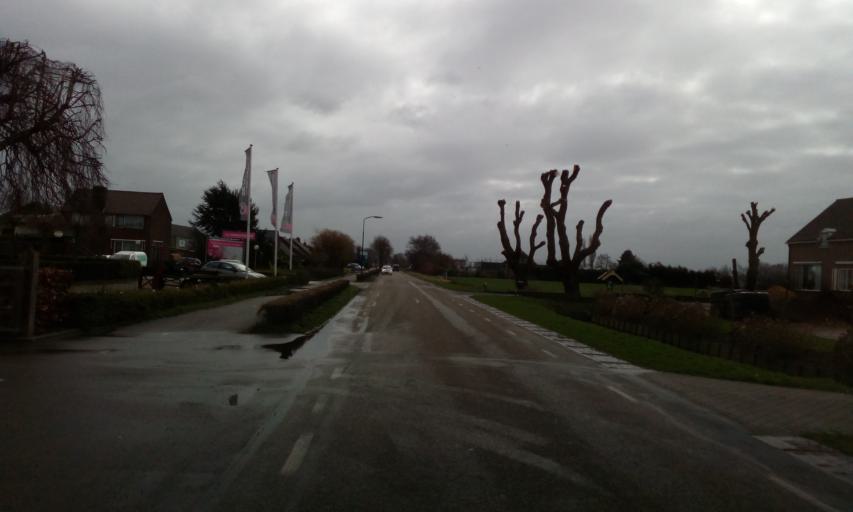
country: NL
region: Utrecht
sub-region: Gemeente De Ronde Venen
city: Mijdrecht
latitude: 52.2067
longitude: 4.8400
